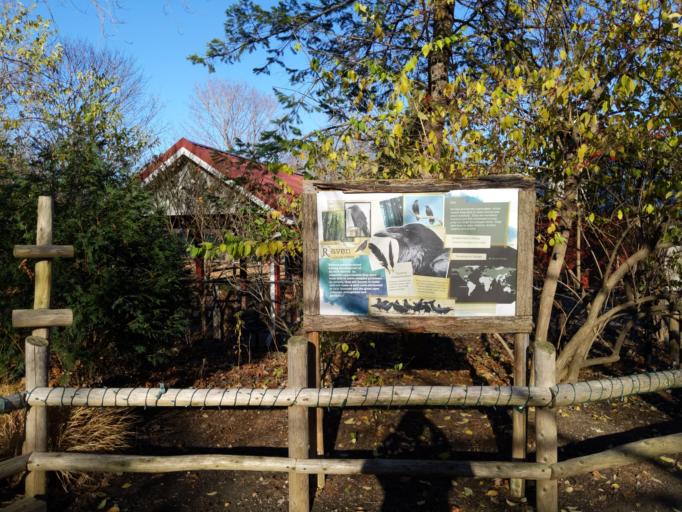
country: US
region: Michigan
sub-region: Ingham County
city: Lansing
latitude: 42.7185
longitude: -84.5264
